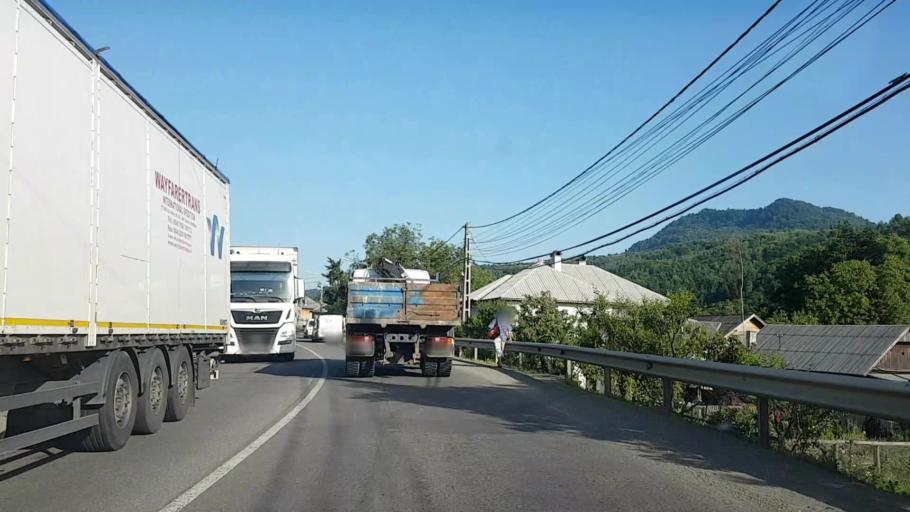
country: RO
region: Bistrita-Nasaud
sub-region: Comuna Tiha Bargaului
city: Tureac
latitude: 47.2280
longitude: 24.8061
